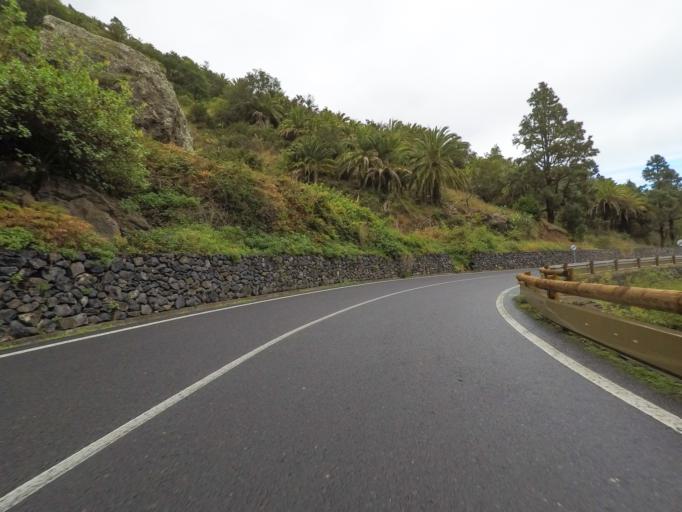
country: ES
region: Canary Islands
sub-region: Provincia de Santa Cruz de Tenerife
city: Hermigua
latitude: 28.1379
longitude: -17.2013
